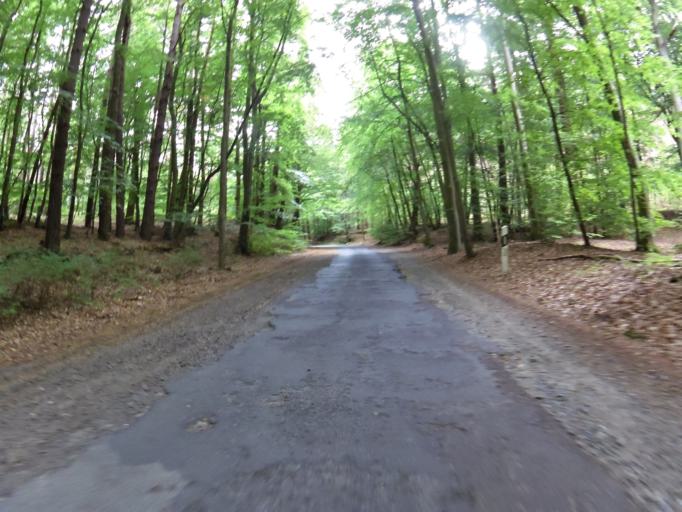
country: DE
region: Mecklenburg-Vorpommern
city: Seebad Heringsdorf
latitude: 53.9496
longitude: 14.1589
